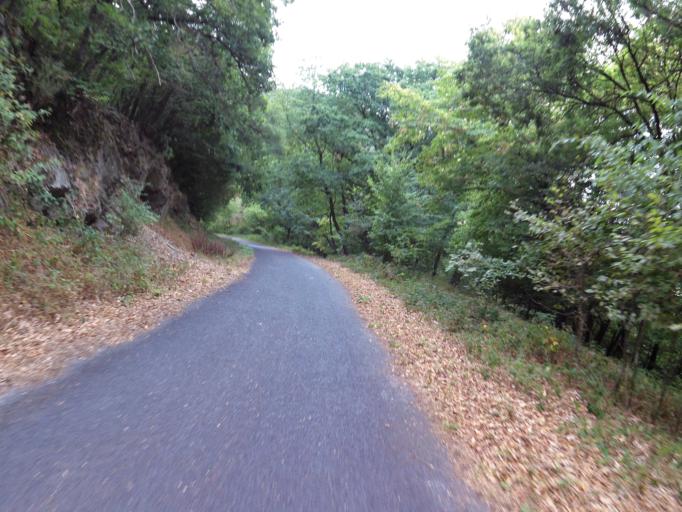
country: DE
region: North Rhine-Westphalia
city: Heimbach
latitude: 50.6208
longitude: 6.3956
